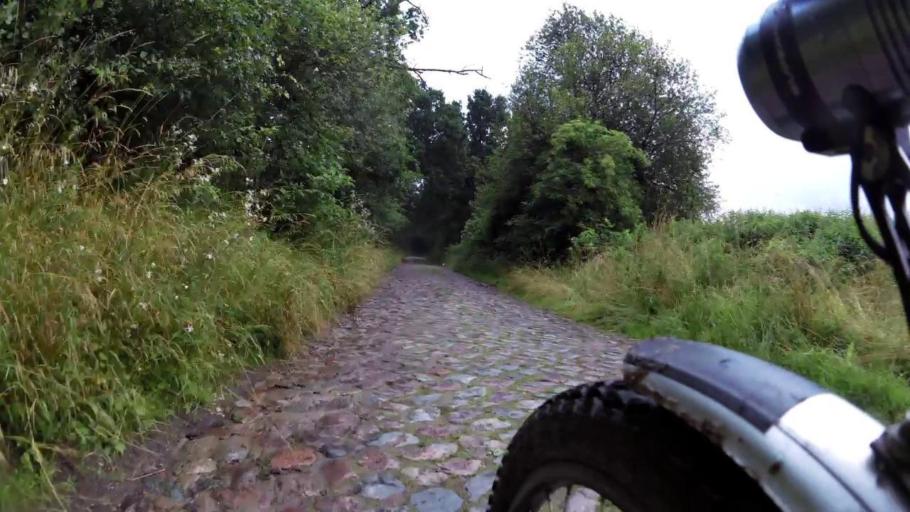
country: PL
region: West Pomeranian Voivodeship
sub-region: Powiat lobeski
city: Lobez
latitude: 53.7302
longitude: 15.6761
